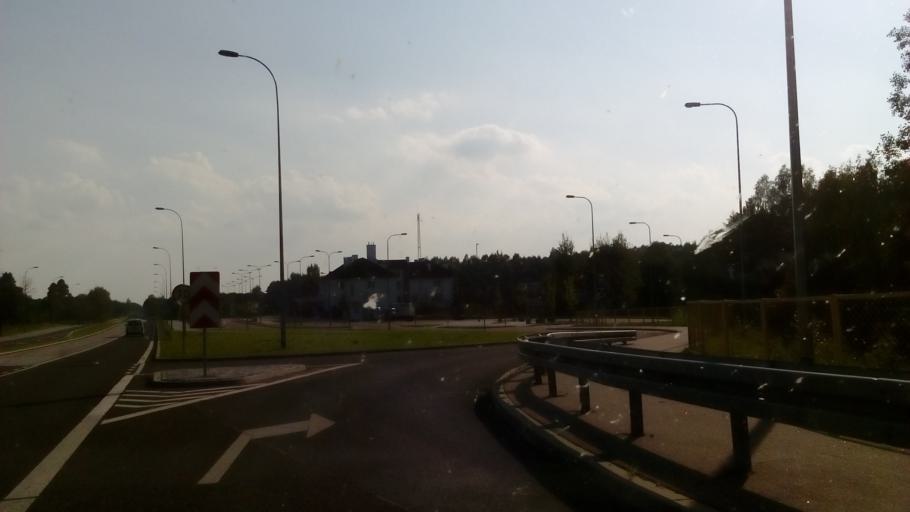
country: LT
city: Lazdijai
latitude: 54.1623
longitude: 23.4747
